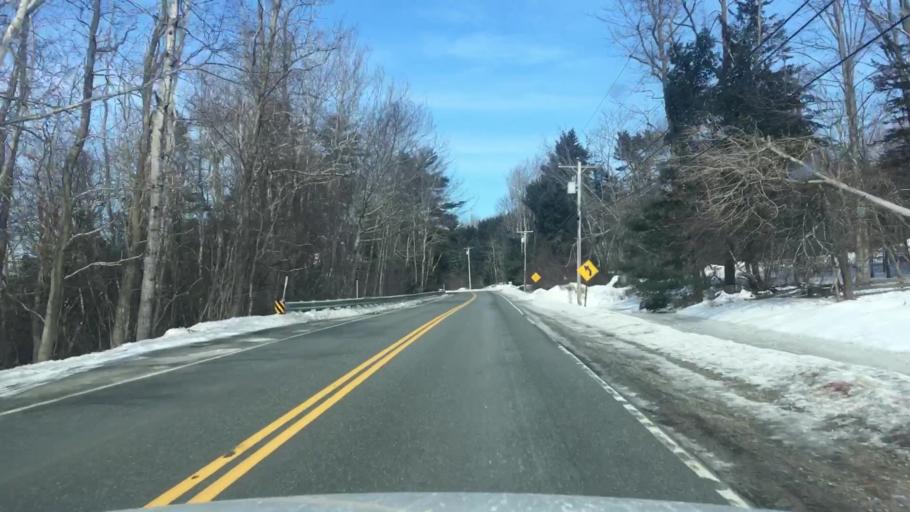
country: US
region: Maine
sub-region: Hancock County
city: Orland
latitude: 44.5438
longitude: -68.7443
